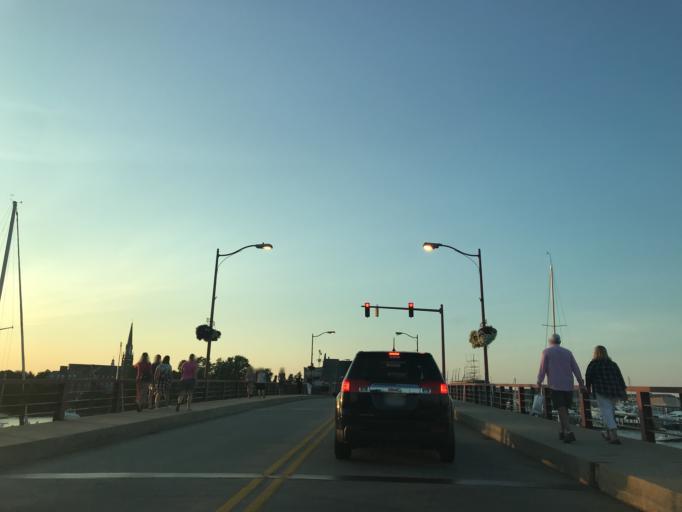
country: US
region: Maryland
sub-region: Anne Arundel County
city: Annapolis
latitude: 38.9720
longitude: -76.4853
